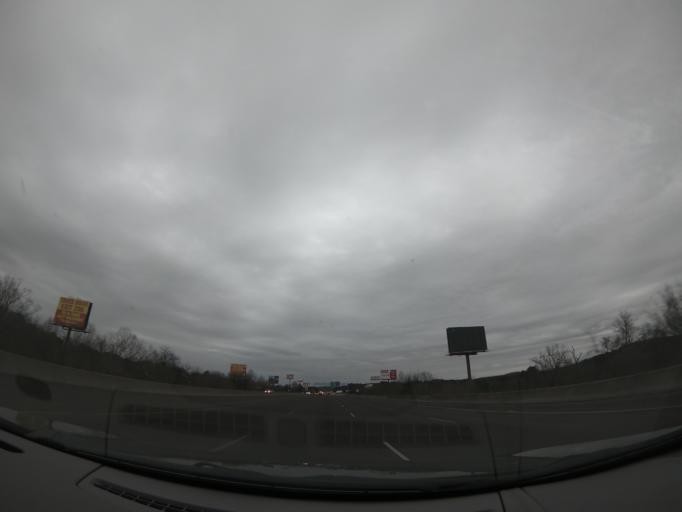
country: US
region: Georgia
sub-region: Gordon County
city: Calhoun
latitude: 34.5718
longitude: -84.9471
